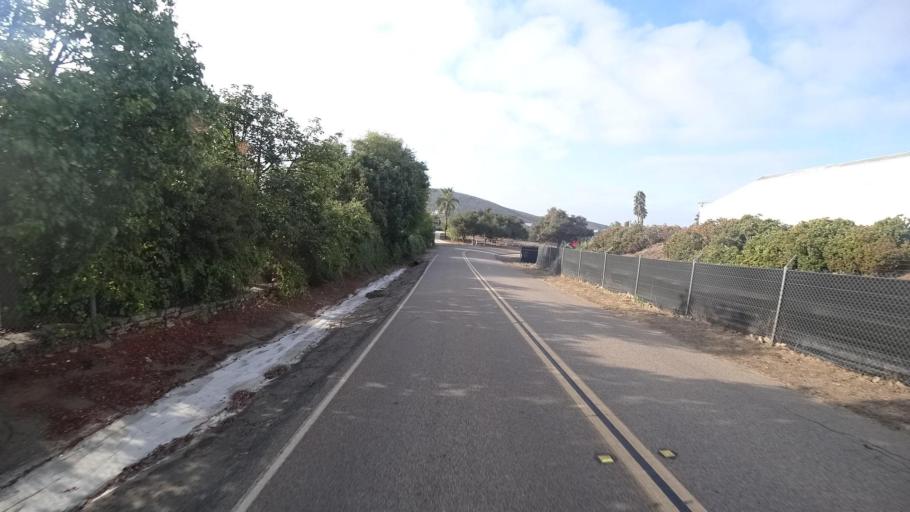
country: US
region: California
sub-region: San Diego County
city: San Marcos
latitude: 33.1817
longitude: -117.1727
